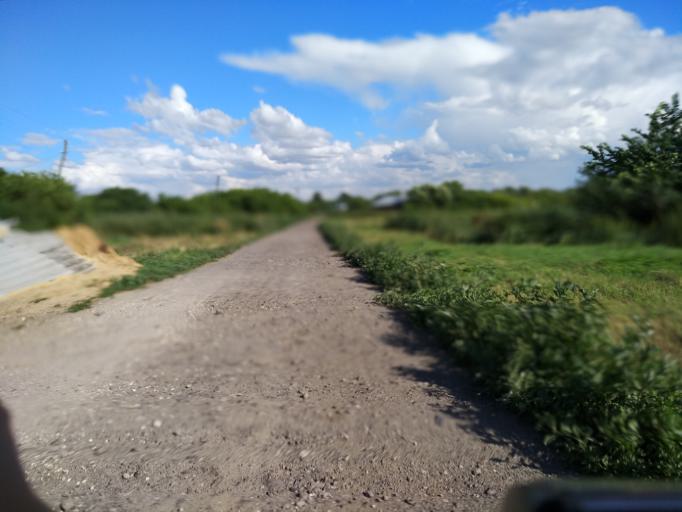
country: RU
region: Lipetsk
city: Dobrinka
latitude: 52.0338
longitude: 40.5612
